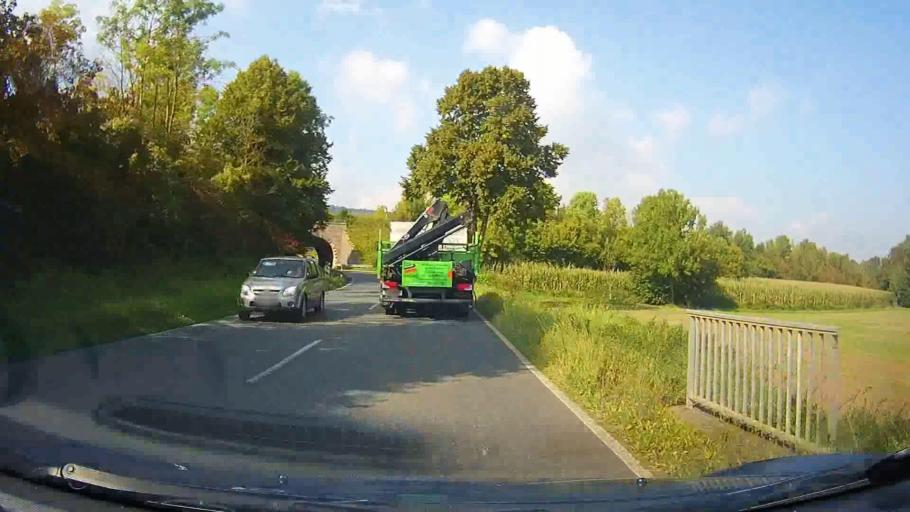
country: DE
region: Lower Saxony
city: Hardegsen
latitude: 51.6572
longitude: 9.8476
